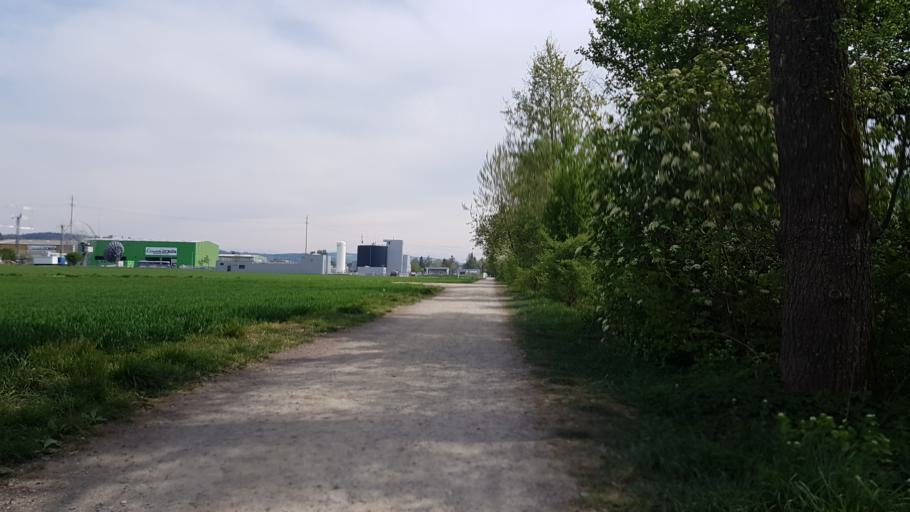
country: CH
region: Aargau
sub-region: Bezirk Kulm
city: Reinach
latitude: 47.2656
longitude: 8.1688
